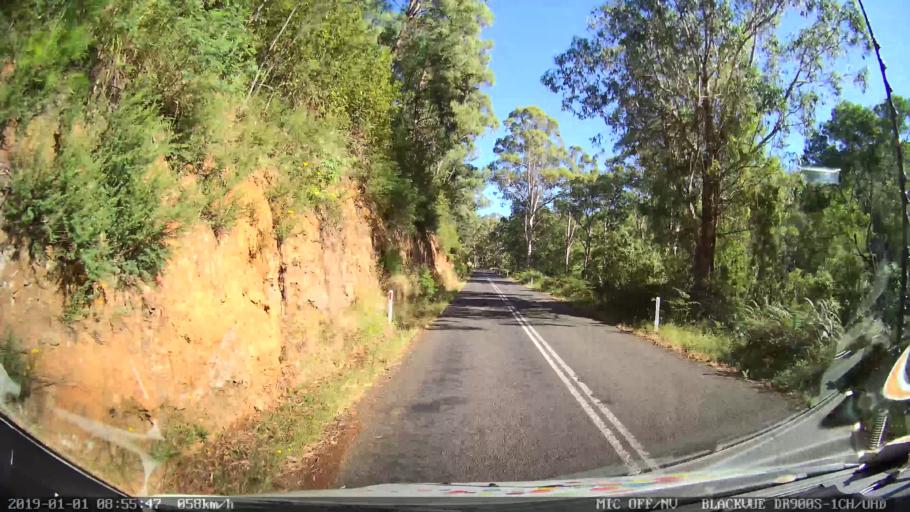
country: AU
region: New South Wales
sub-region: Snowy River
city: Jindabyne
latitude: -36.2514
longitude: 148.1906
